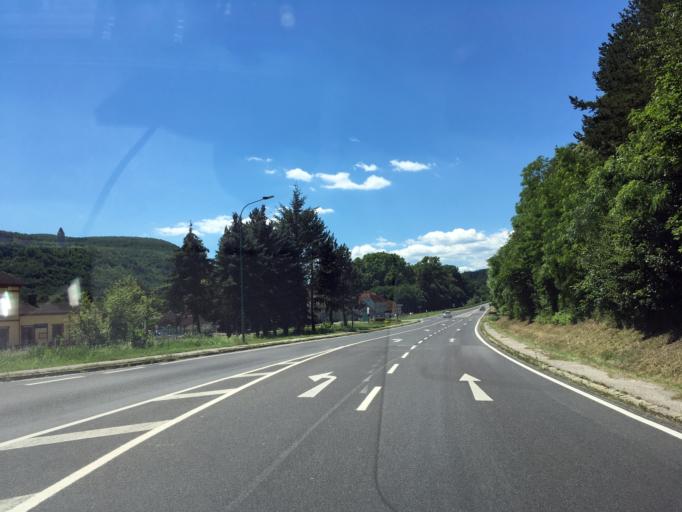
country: AT
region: Lower Austria
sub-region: Politischer Bezirk Neunkirchen
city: Seebenstein
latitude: 47.7041
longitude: 16.1429
